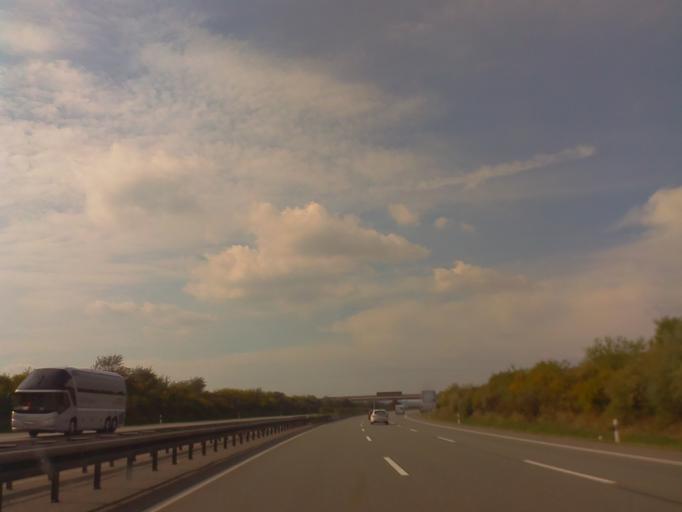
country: DE
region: Thuringia
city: Horselgau
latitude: 50.9063
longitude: 10.6049
